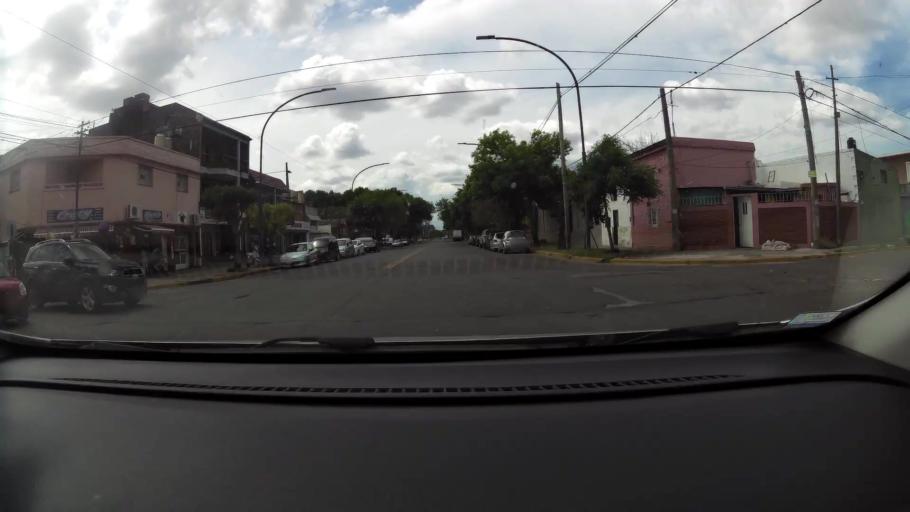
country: AR
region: Santa Fe
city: Gobernador Galvez
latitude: -32.9984
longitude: -60.6365
